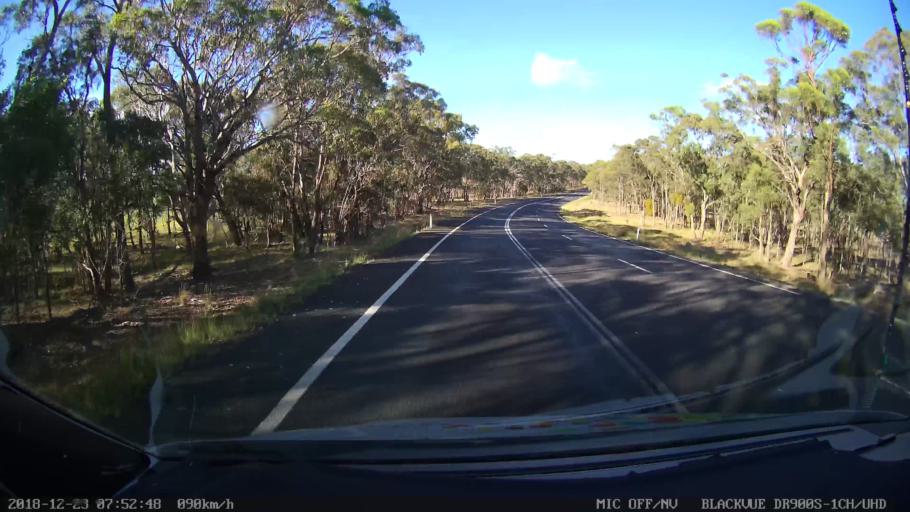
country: AU
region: New South Wales
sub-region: Armidale Dumaresq
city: Armidale
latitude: -30.5319
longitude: 151.8165
